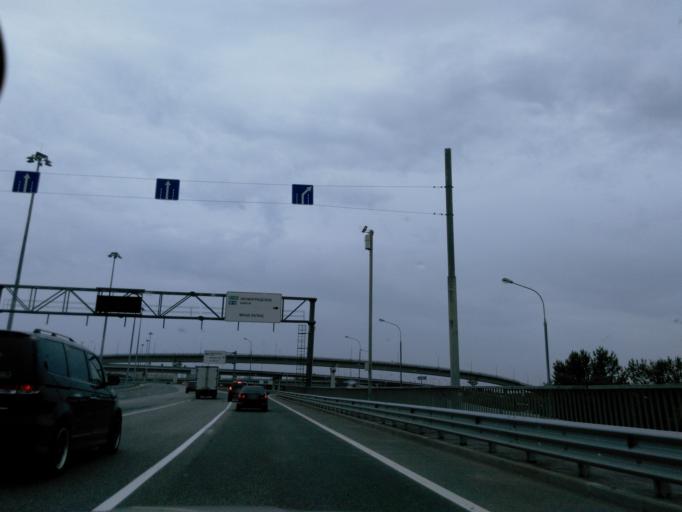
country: RU
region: Moskovskaya
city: Levoberezhnaya
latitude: 55.8894
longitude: 37.4834
